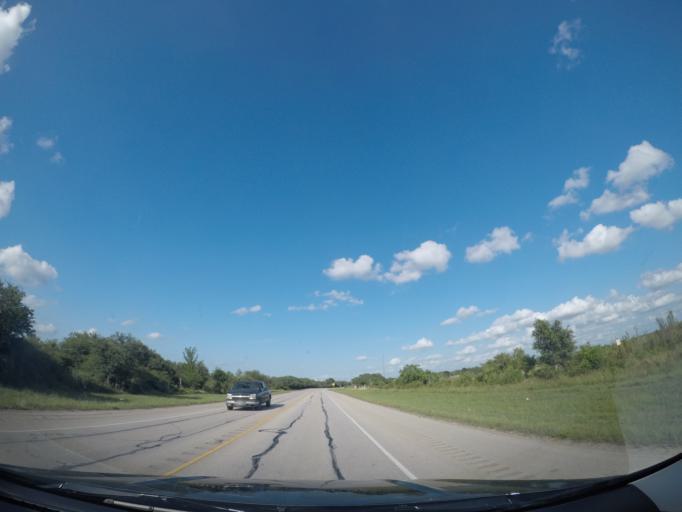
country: US
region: Texas
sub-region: Colorado County
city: Eagle Lake
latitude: 29.5682
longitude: -96.4754
